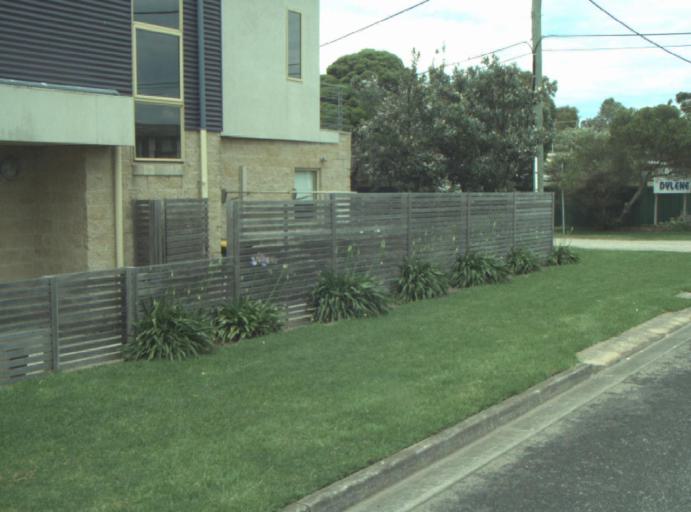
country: AU
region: Victoria
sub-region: Greater Geelong
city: Clifton Springs
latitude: -38.1144
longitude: 144.6702
